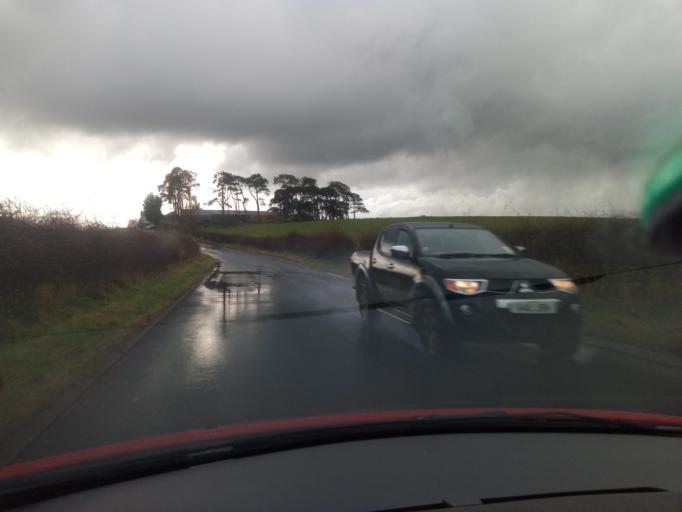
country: GB
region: England
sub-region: Northumberland
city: Birtley
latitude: 55.1144
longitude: -2.2405
